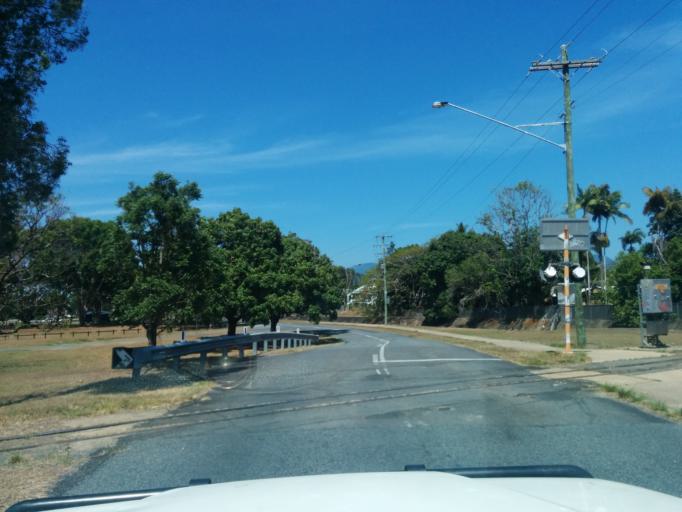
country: AU
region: Queensland
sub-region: Cairns
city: Woree
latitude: -16.9474
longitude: 145.7363
